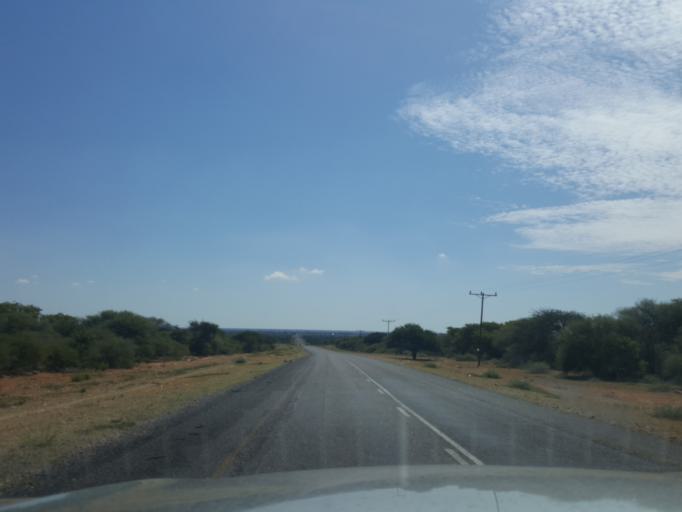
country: BW
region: Kweneng
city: Letlhakeng
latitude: -24.1217
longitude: 25.0837
